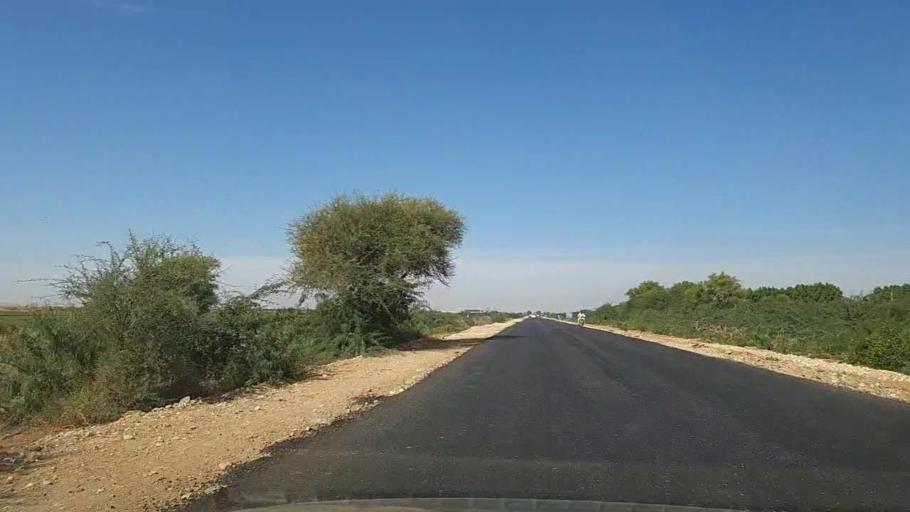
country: PK
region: Sindh
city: Kotri
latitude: 25.2350
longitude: 68.2332
